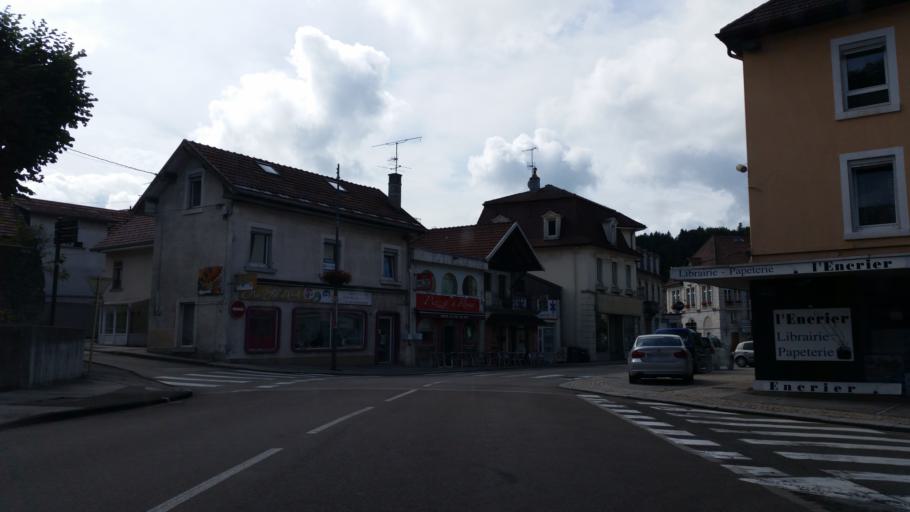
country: FR
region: Franche-Comte
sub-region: Departement du Doubs
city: Maiche
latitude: 47.2535
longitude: 6.8018
